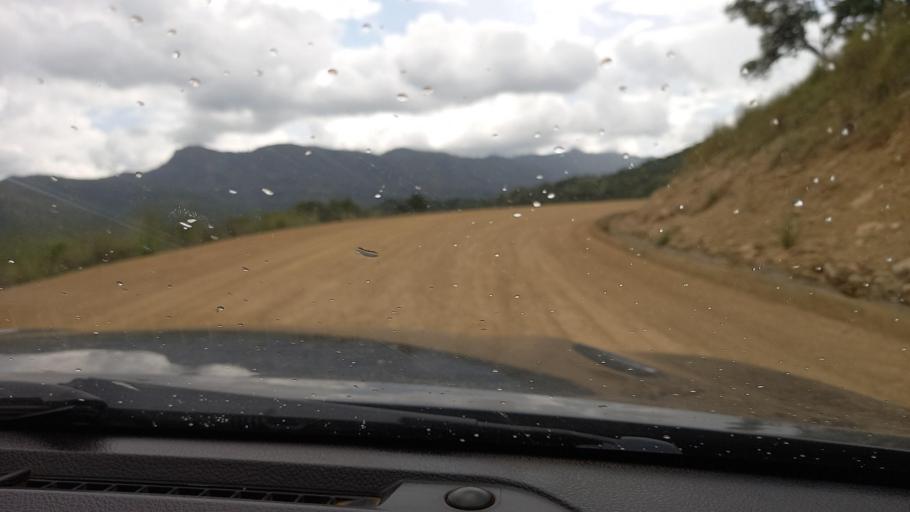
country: ET
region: Southern Nations, Nationalities, and People's Region
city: Mizan Teferi
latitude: 6.2039
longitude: 35.6717
